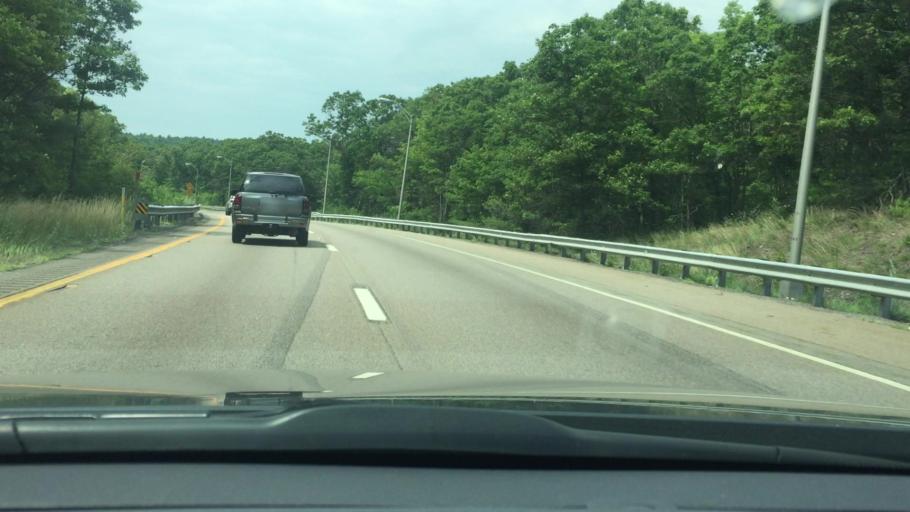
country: US
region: Massachusetts
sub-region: Norfolk County
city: Milton
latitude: 42.2001
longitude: -71.0783
